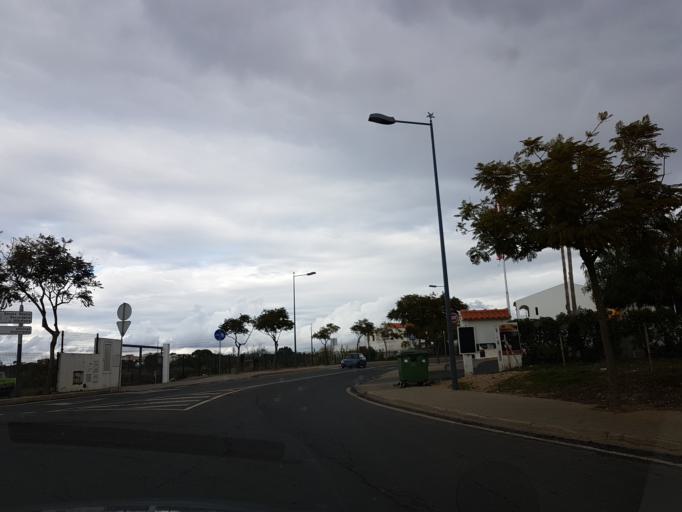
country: PT
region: Faro
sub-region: Albufeira
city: Ferreiras
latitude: 37.1090
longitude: -8.2308
